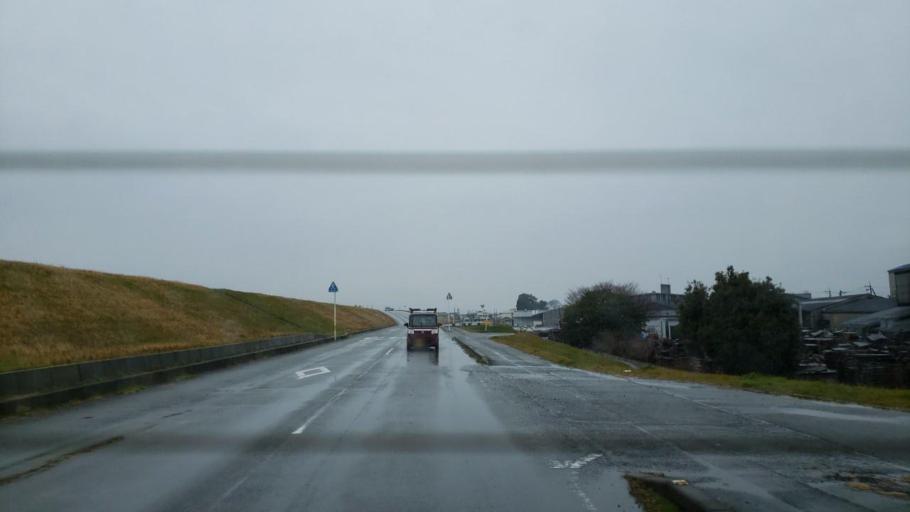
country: JP
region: Tokushima
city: Ishii
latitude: 34.1063
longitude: 134.4267
